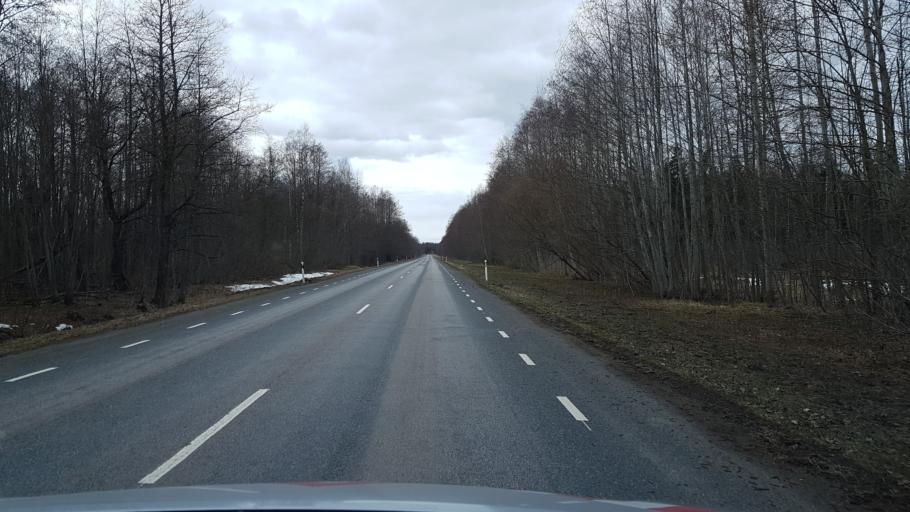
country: EE
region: Ida-Virumaa
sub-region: Narva-Joesuu linn
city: Narva-Joesuu
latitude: 59.3519
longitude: 28.0623
